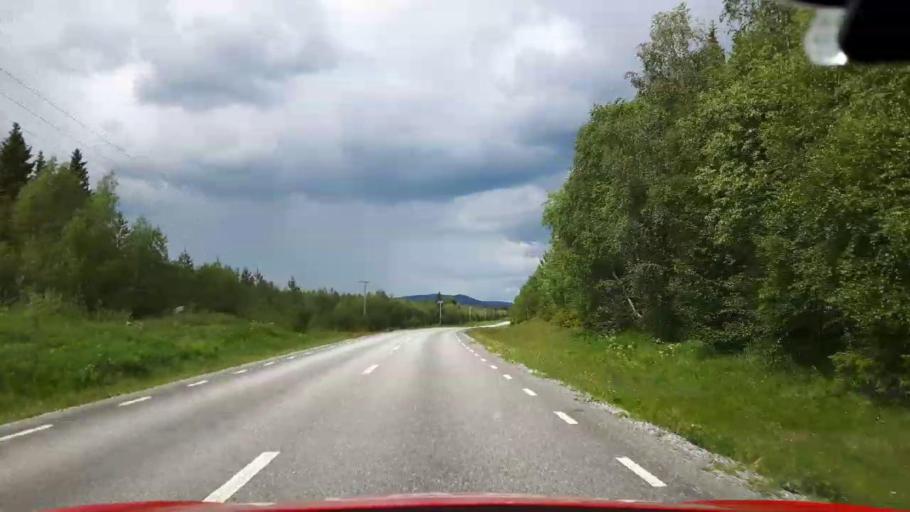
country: SE
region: Jaemtland
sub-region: Krokoms Kommun
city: Krokom
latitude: 63.6530
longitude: 14.3719
